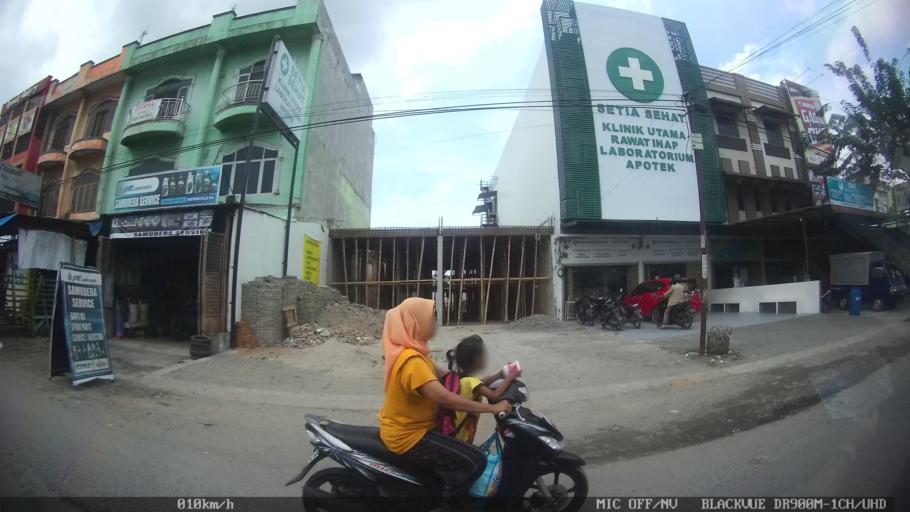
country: ID
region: North Sumatra
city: Labuhan Deli
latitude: 3.6920
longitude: 98.6561
